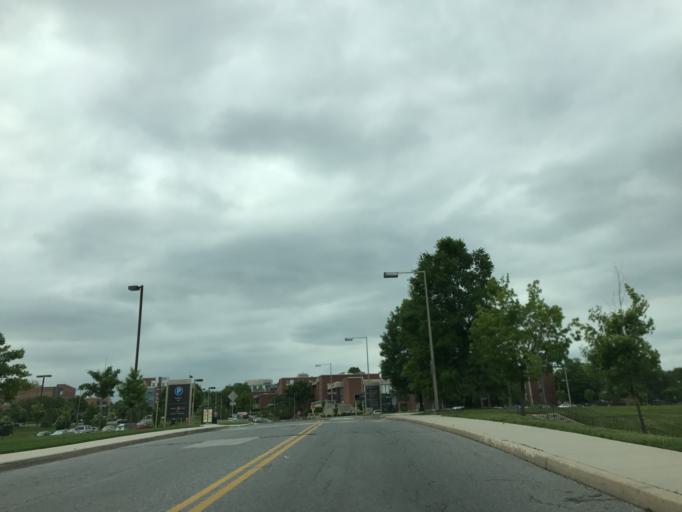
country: US
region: Maryland
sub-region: Baltimore County
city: Arbutus
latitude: 39.2539
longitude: -76.7047
